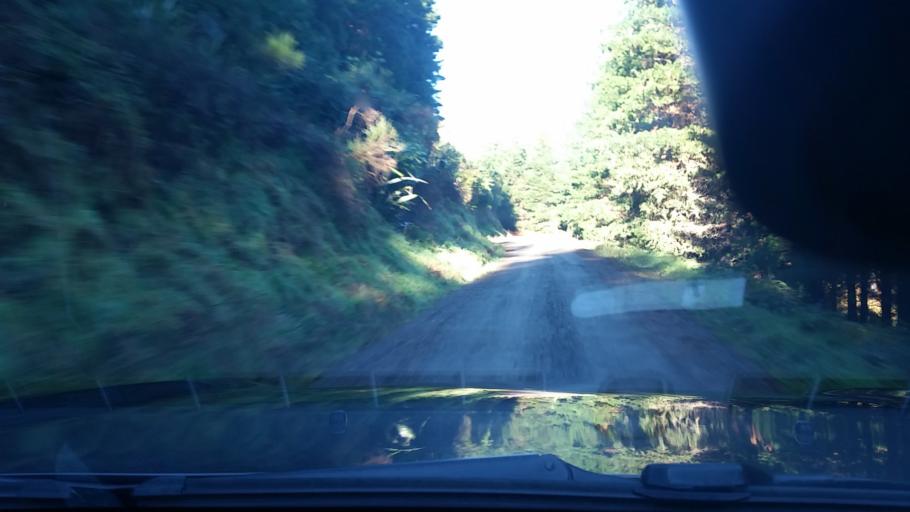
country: NZ
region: Marlborough
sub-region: Marlborough District
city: Blenheim
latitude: -41.6245
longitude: 173.9665
